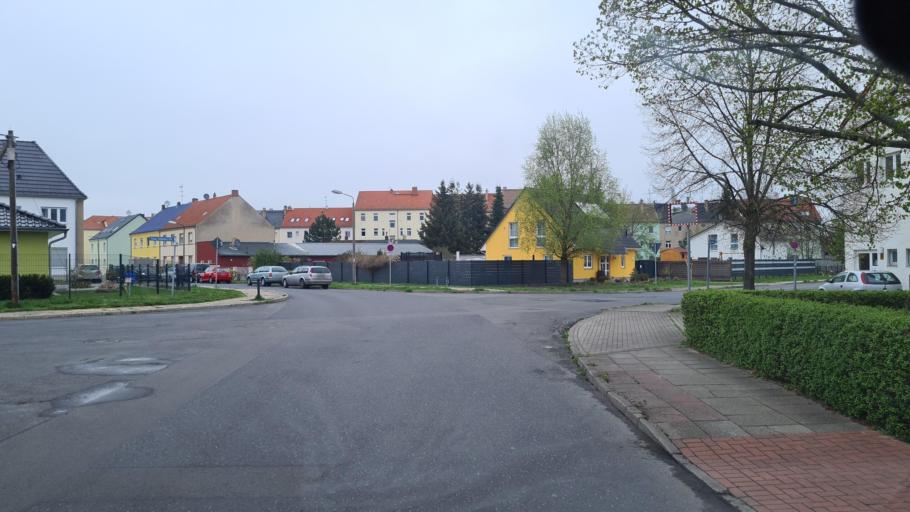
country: DE
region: Brandenburg
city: Luckenwalde
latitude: 52.0883
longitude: 13.1554
